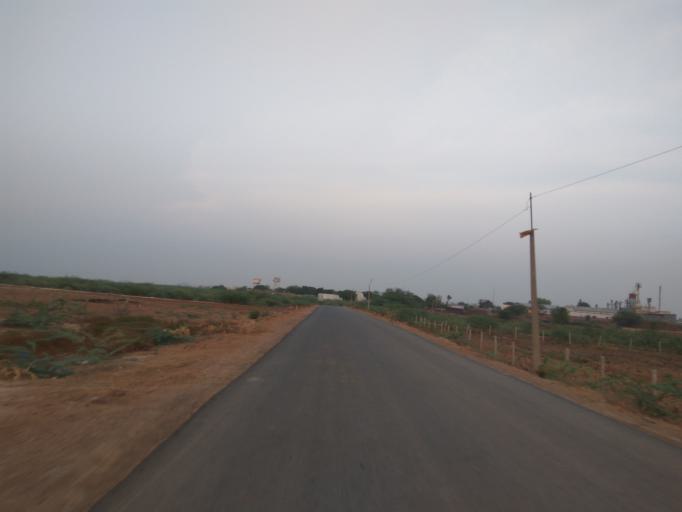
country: IN
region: Andhra Pradesh
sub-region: Prakasam
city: Markapur
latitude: 15.7405
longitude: 79.2494
